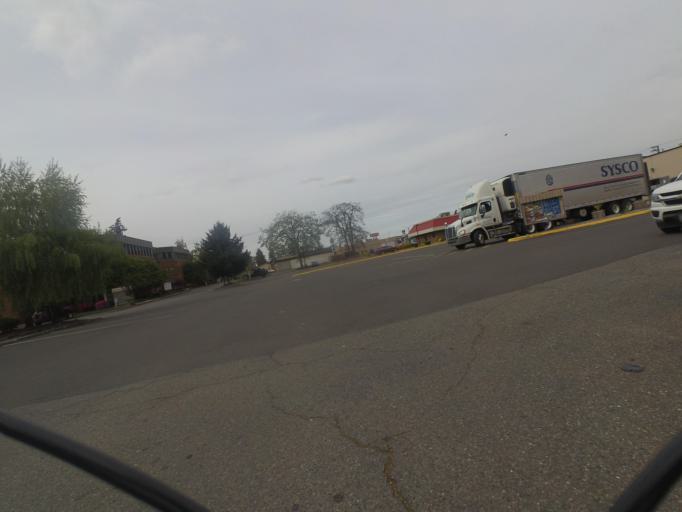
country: US
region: Washington
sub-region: Pierce County
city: McChord Air Force Base
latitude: 47.1651
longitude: -122.4848
